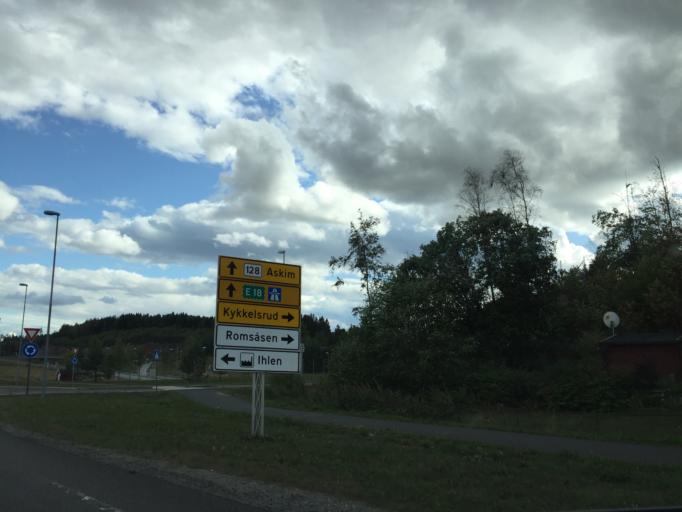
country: NO
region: Ostfold
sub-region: Spydeberg
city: Spydeberg
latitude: 59.5891
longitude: 11.1133
